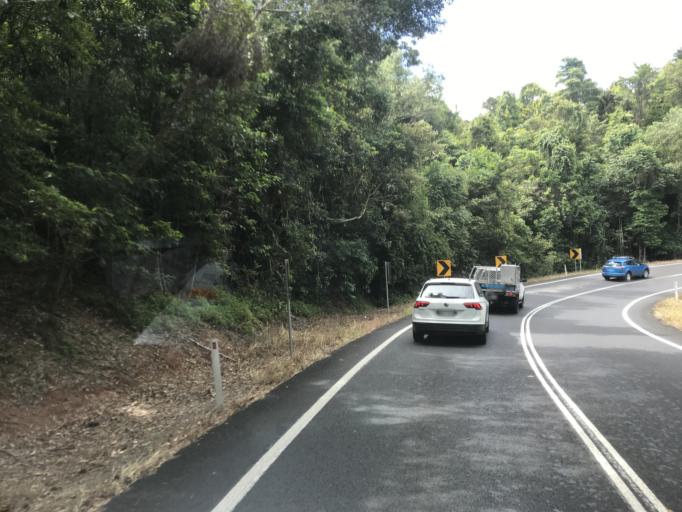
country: AU
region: Queensland
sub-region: Cassowary Coast
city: Innisfail
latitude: -17.8679
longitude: 146.0719
